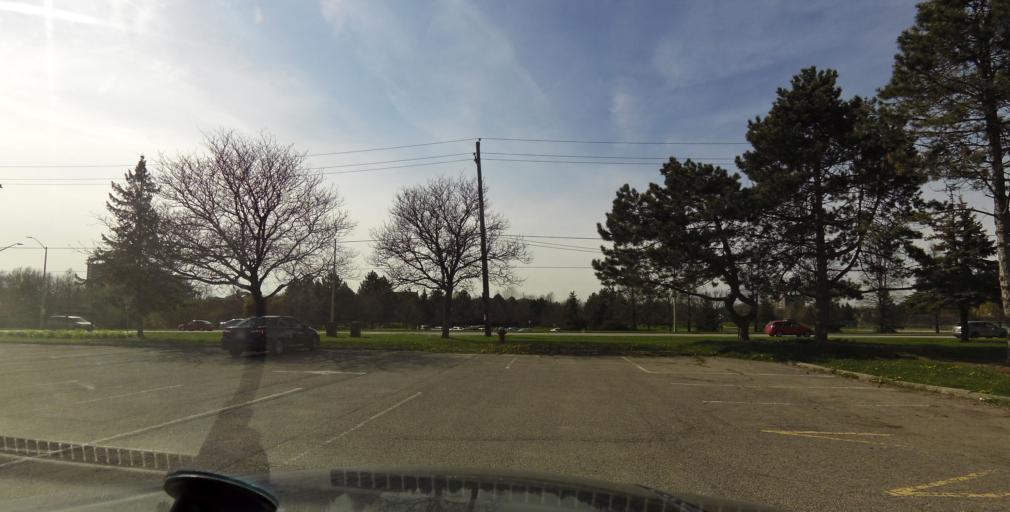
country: CA
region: Ontario
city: Etobicoke
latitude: 43.6350
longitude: -79.5880
